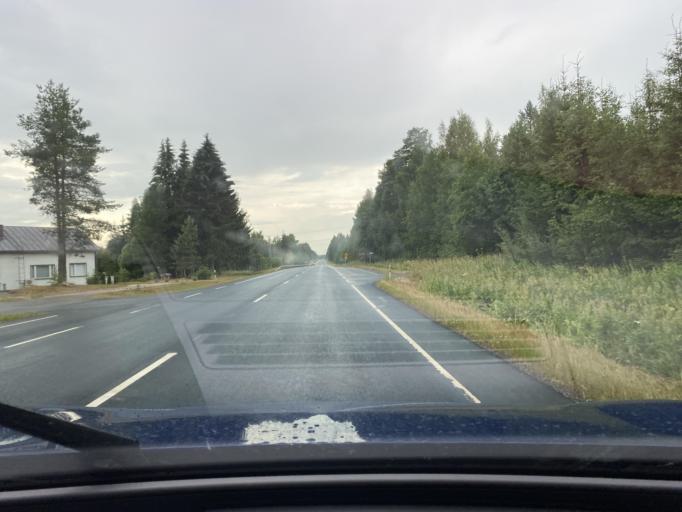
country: FI
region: Central Ostrobothnia
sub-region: Kaustinen
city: Veteli
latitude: 63.4181
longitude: 23.9411
